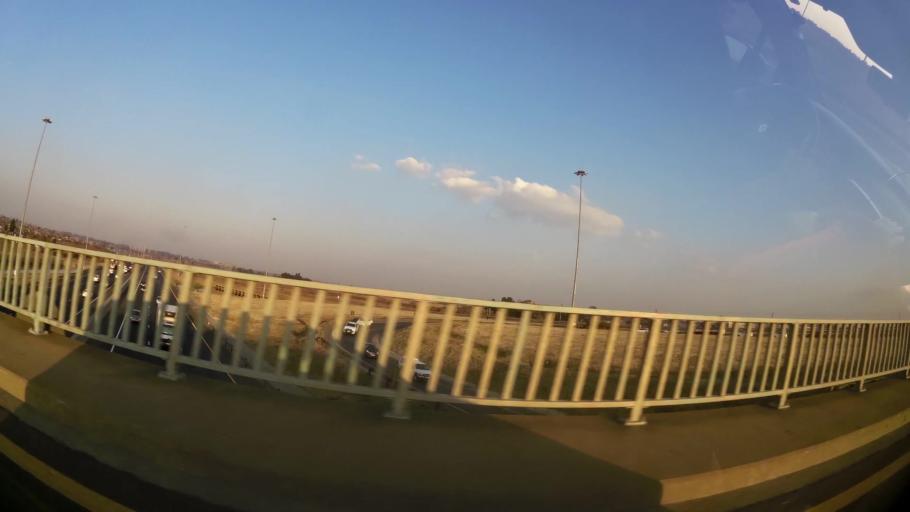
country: ZA
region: Gauteng
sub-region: Ekurhuleni Metropolitan Municipality
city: Benoni
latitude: -26.1648
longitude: 28.3691
